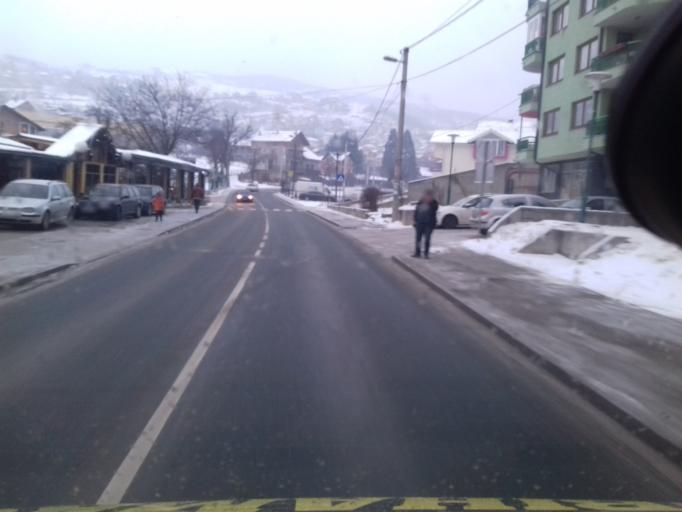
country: BA
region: Federation of Bosnia and Herzegovina
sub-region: Kanton Sarajevo
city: Sarajevo
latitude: 43.8575
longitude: 18.3659
